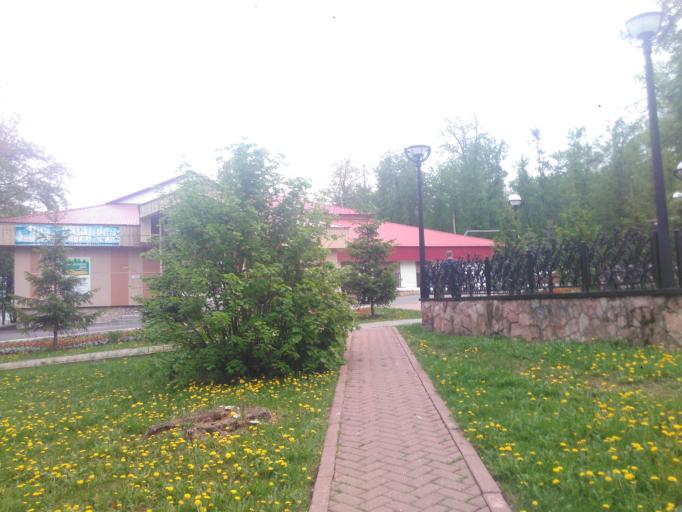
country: RU
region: Tatarstan
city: Al'met'yevsk
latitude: 54.9523
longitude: 52.2664
